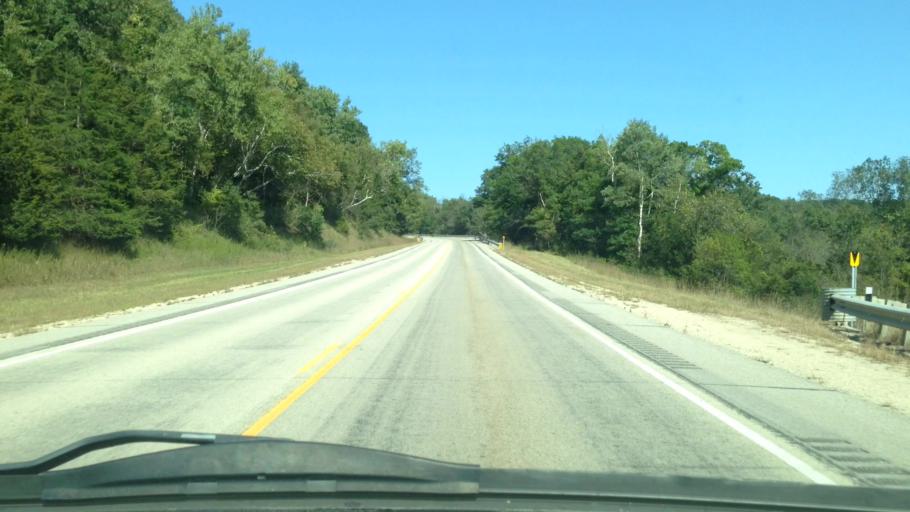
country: US
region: Minnesota
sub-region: Fillmore County
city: Rushford
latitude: 43.8358
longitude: -91.7603
